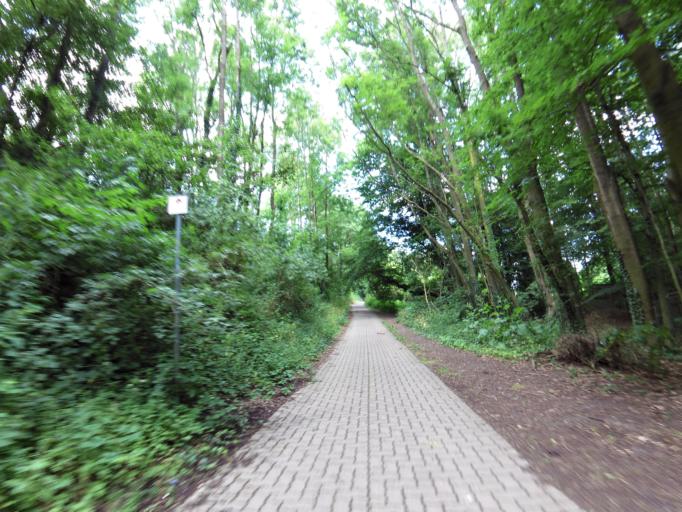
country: DE
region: North Rhine-Westphalia
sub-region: Regierungsbezirk Koln
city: Herzogenrath
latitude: 50.8557
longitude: 6.0873
